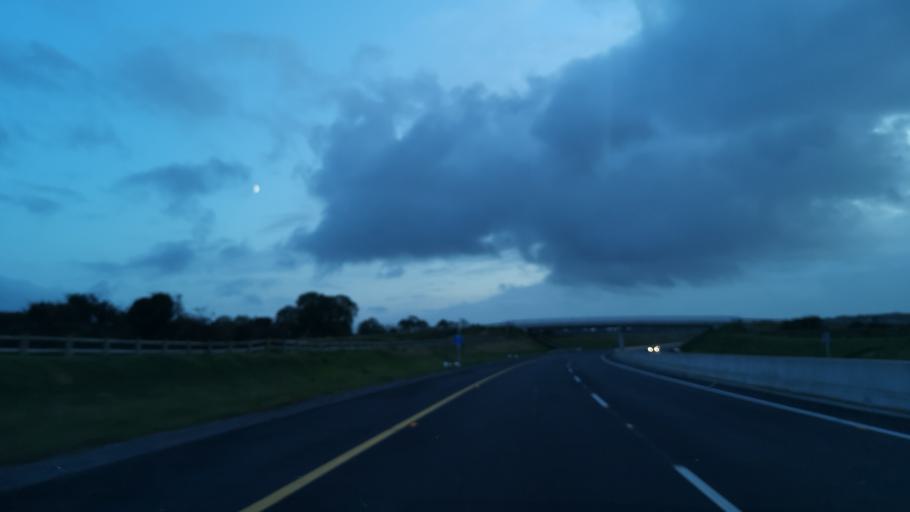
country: IE
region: Connaught
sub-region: County Galway
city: Athenry
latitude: 53.3621
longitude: -8.7882
